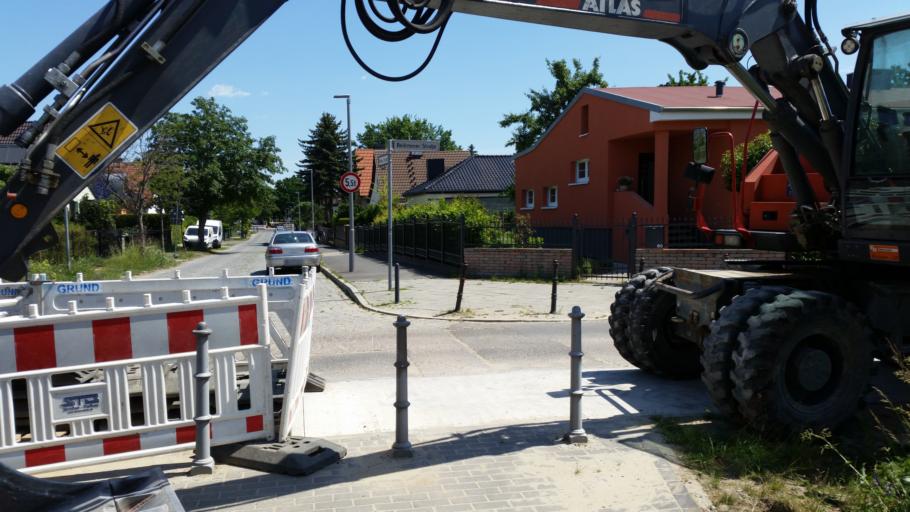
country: DE
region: Berlin
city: Friedrichsfelde
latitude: 52.5199
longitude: 13.5277
